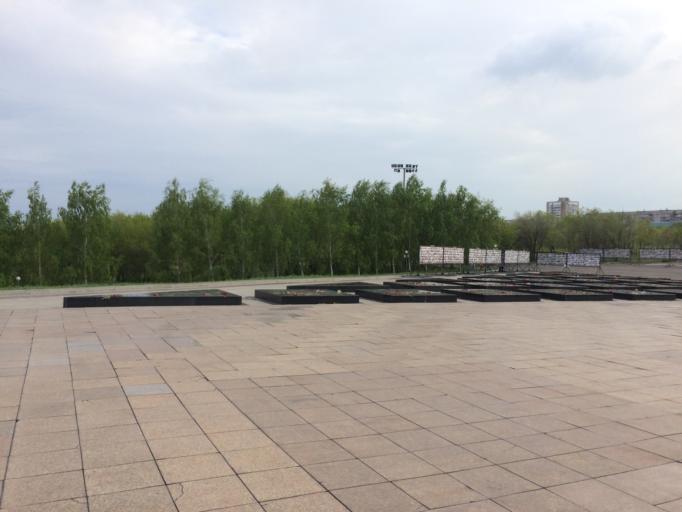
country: RU
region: Chelyabinsk
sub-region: Gorod Magnitogorsk
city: Magnitogorsk
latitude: 53.4072
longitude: 58.9922
